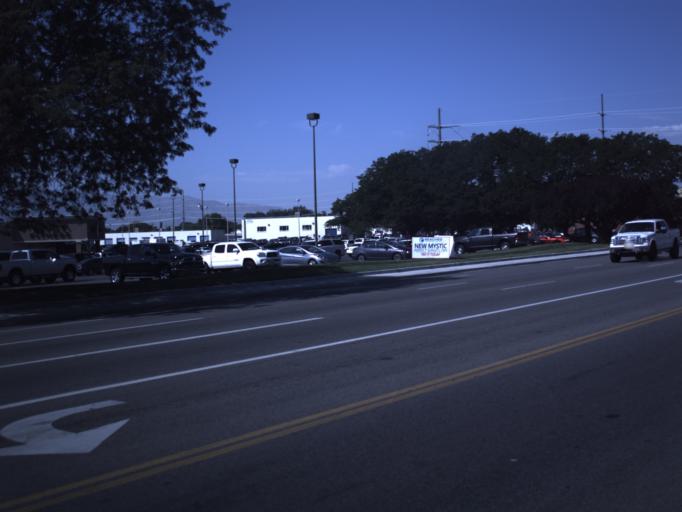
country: US
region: Utah
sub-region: Utah County
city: American Fork
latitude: 40.3729
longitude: -111.7809
